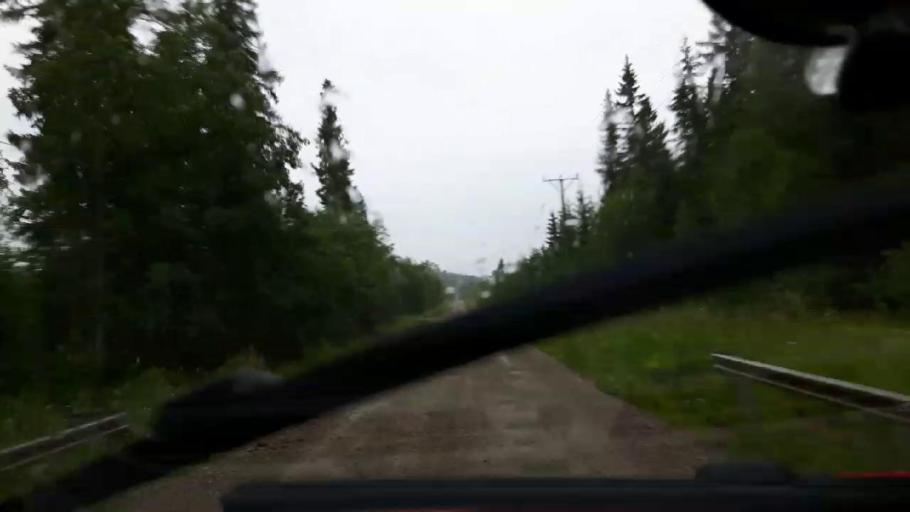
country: SE
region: Jaemtland
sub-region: OEstersunds Kommun
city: Brunflo
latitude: 62.7777
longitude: 14.9836
